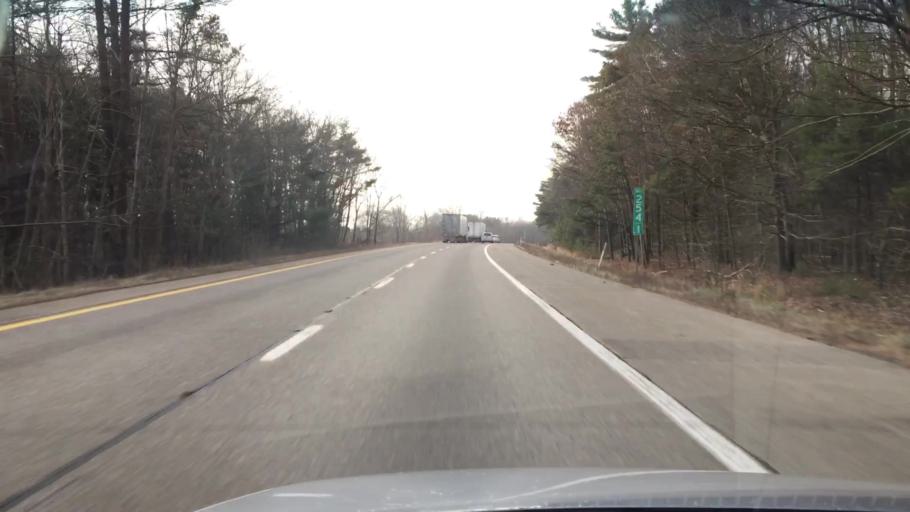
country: US
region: Pennsylvania
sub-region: Luzerne County
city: Conyngham
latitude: 41.0193
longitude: -76.1118
